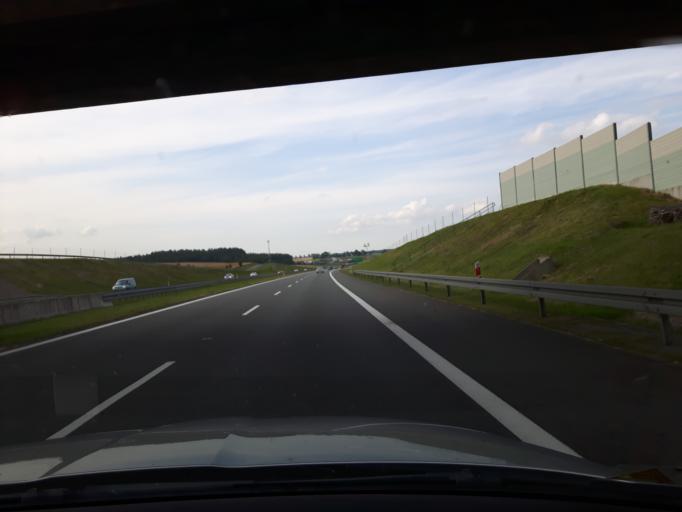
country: PL
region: Warmian-Masurian Voivodeship
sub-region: Powiat ostrodzki
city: Maldyty
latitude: 53.8735
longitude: 19.7393
